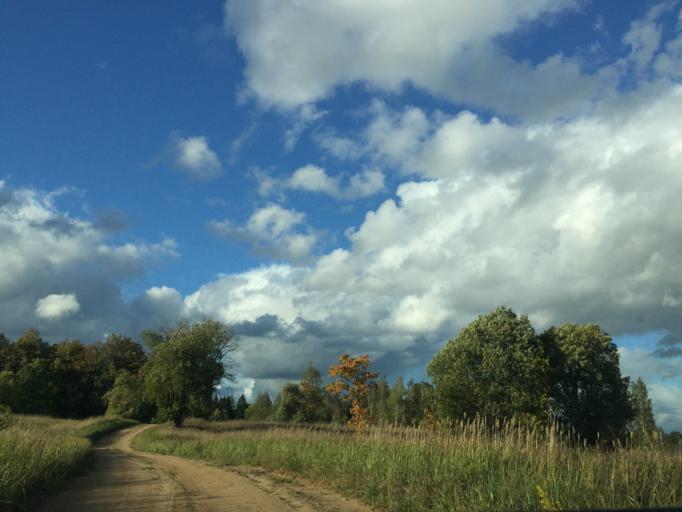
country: LV
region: Ligatne
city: Ligatne
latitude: 57.1288
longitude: 25.1263
